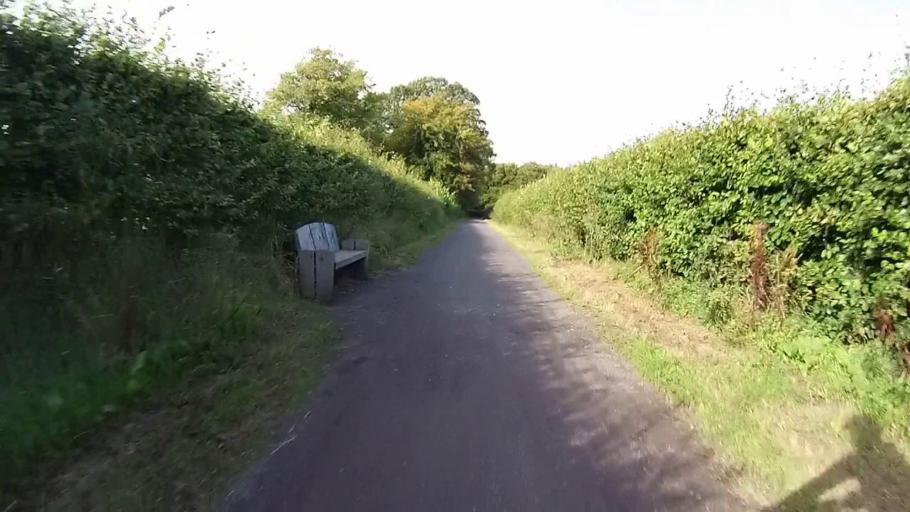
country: GB
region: Scotland
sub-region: Perth and Kinross
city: Kinross
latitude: 56.2027
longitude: -3.4067
